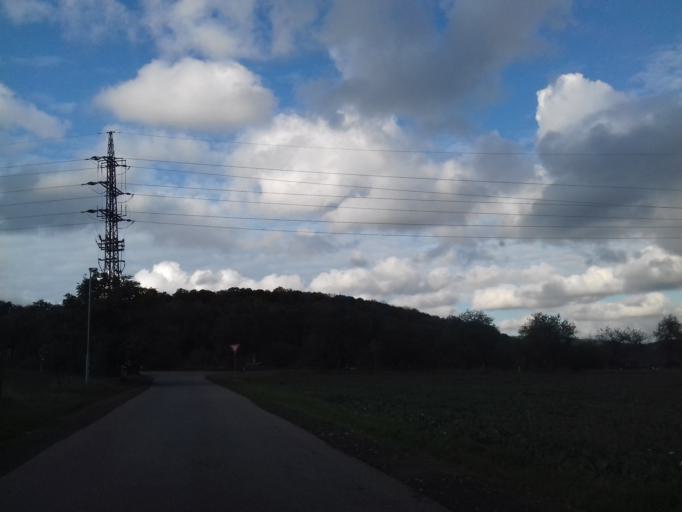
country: CZ
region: Central Bohemia
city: Revnice
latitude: 49.9250
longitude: 14.2419
